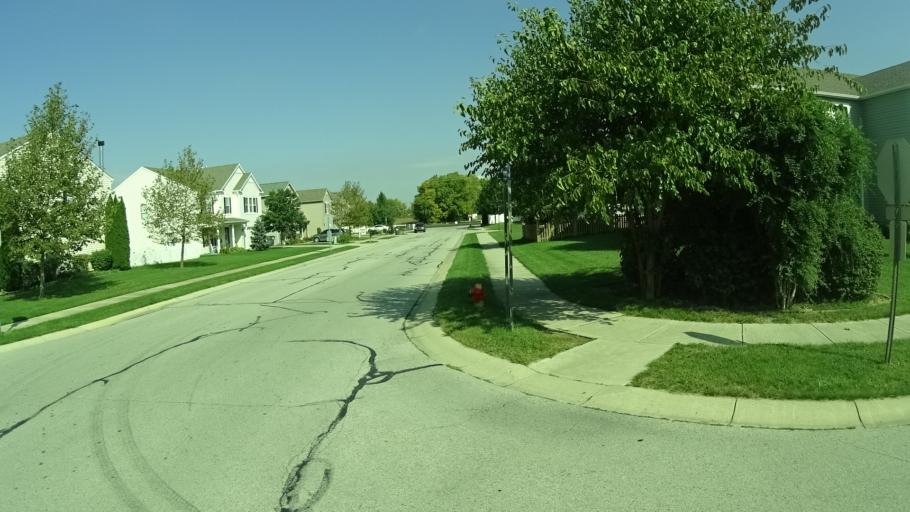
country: US
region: Indiana
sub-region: Hancock County
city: Fortville
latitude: 39.9864
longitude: -85.8550
